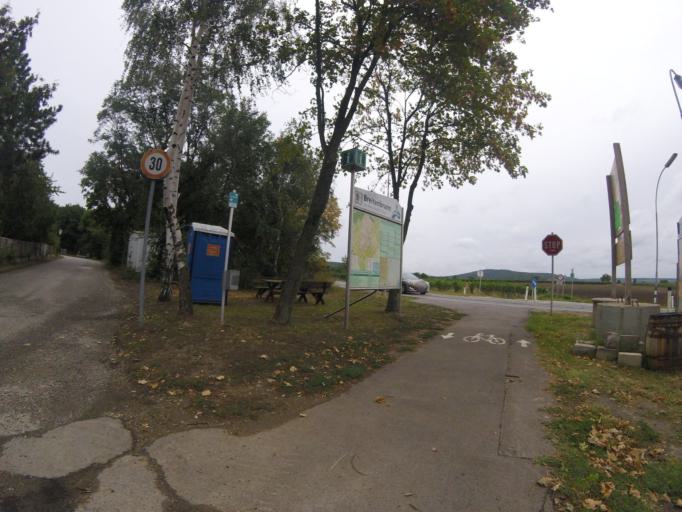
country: AT
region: Burgenland
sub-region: Politischer Bezirk Neusiedl am See
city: Winden am See
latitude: 47.9537
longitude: 16.7394
